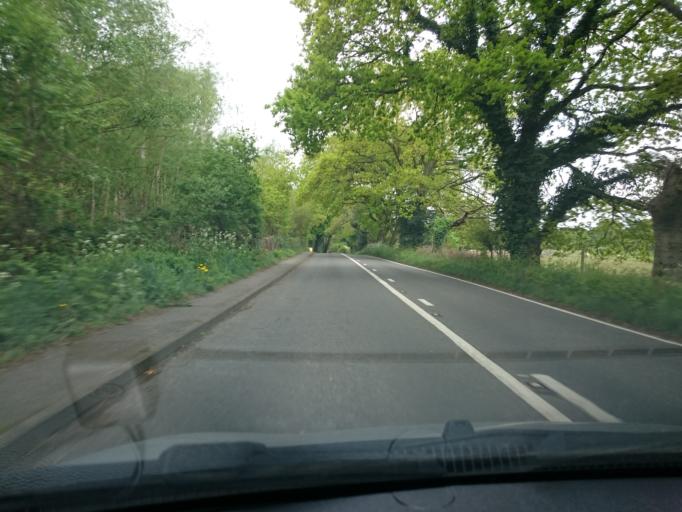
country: GB
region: England
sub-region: Surrey
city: Normandy
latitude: 51.2543
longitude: -0.6895
